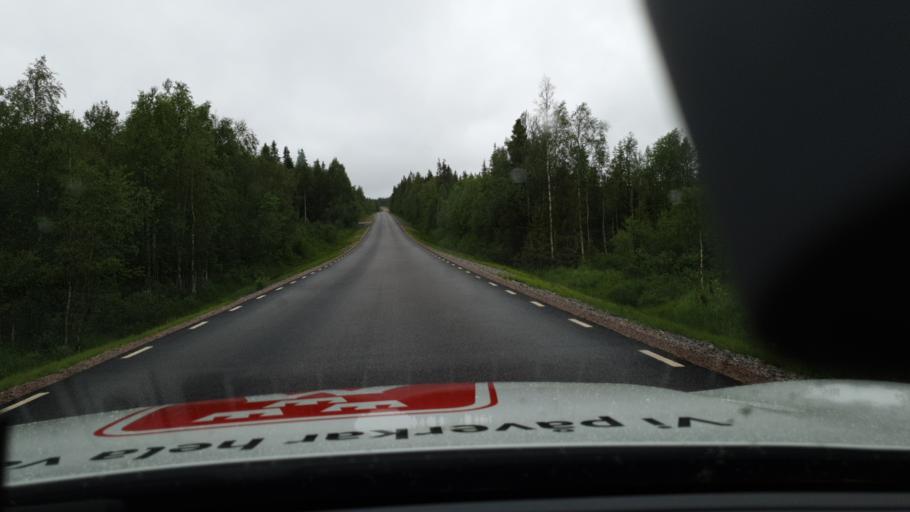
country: SE
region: Norrbotten
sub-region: Overtornea Kommun
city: OEvertornea
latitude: 66.4975
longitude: 23.4298
